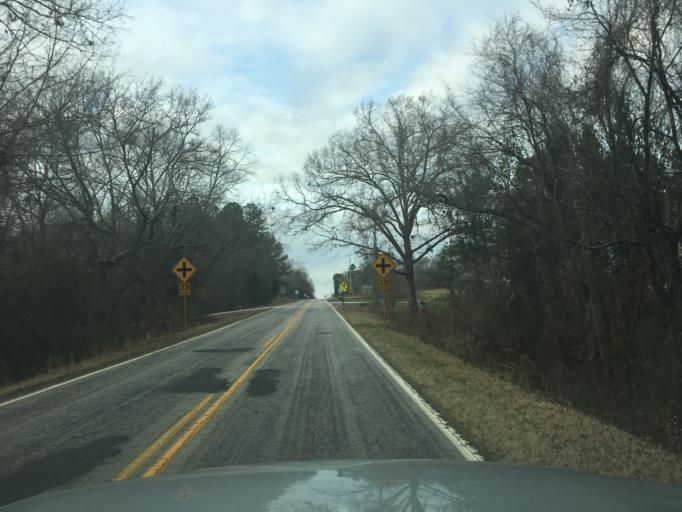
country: US
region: South Carolina
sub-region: Abbeville County
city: Due West
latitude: 34.2978
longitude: -82.4508
